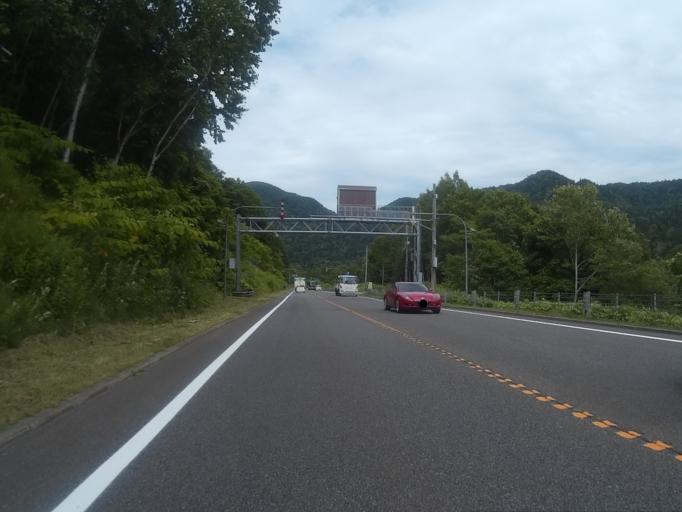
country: JP
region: Hokkaido
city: Sapporo
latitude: 42.9120
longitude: 141.1204
